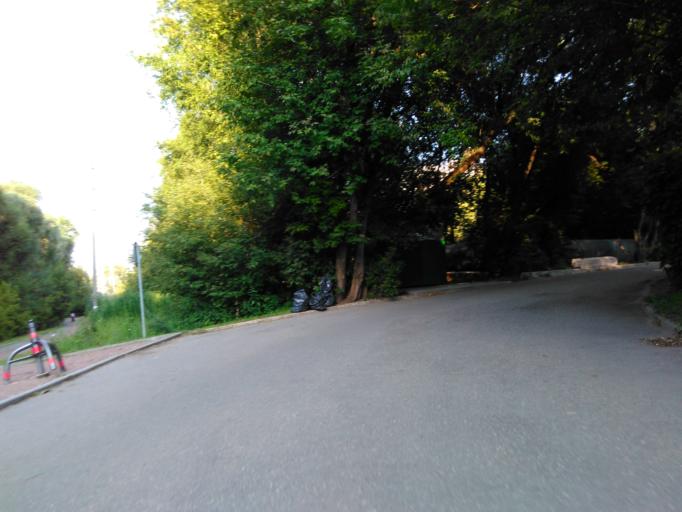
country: RU
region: Moscow
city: Vorob'yovo
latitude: 55.7291
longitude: 37.5217
